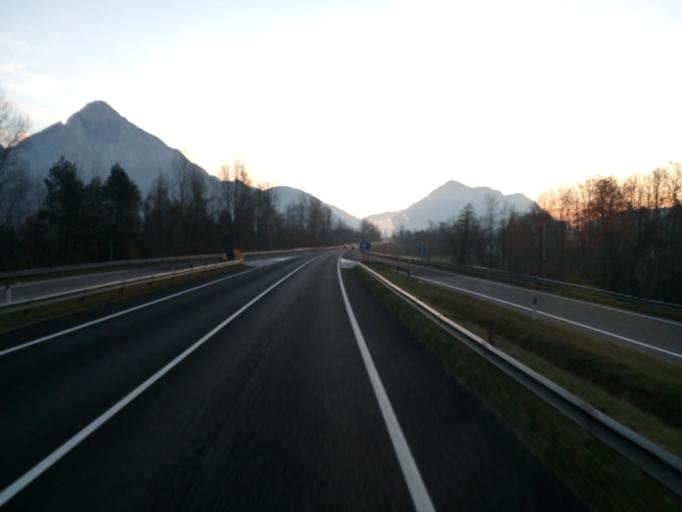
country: IT
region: Friuli Venezia Giulia
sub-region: Provincia di Udine
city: Chiaulis
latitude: 46.4052
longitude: 12.9915
